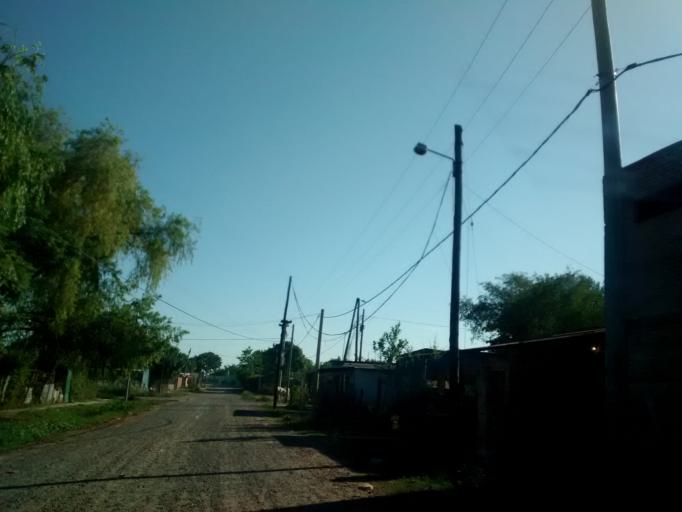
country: AR
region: Chaco
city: Resistencia
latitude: -27.4607
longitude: -58.9612
